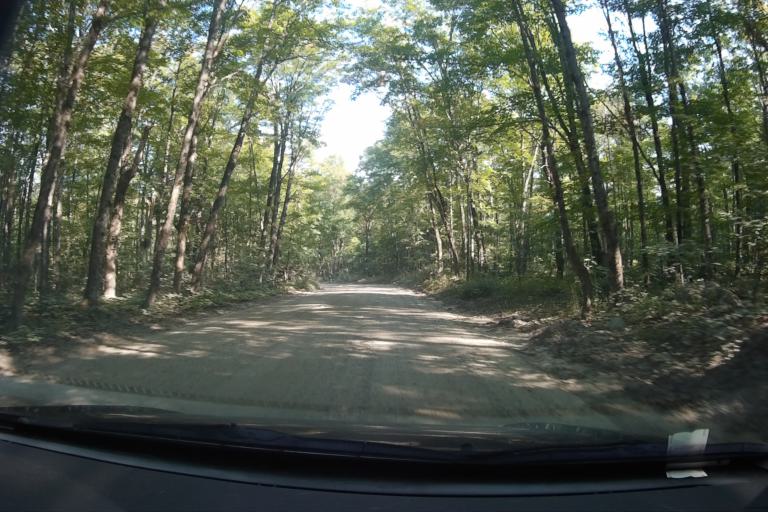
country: CA
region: Ontario
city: Huntsville
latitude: 45.5584
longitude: -78.6950
